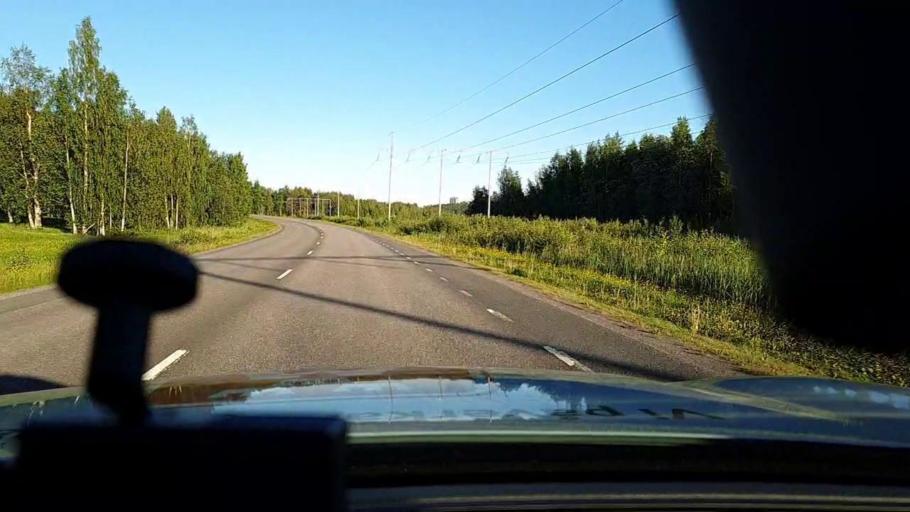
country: SE
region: Norrbotten
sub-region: Lulea Kommun
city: Lulea
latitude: 65.6095
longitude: 22.1663
